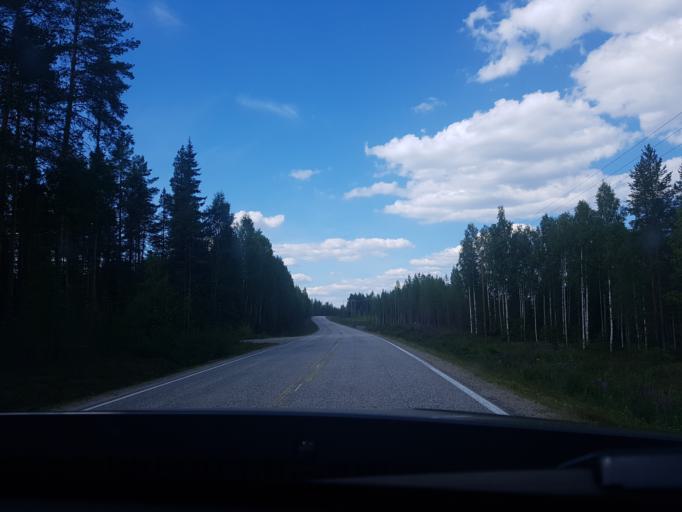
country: FI
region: Kainuu
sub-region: Kehys-Kainuu
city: Kuhmo
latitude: 64.2414
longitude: 29.8126
